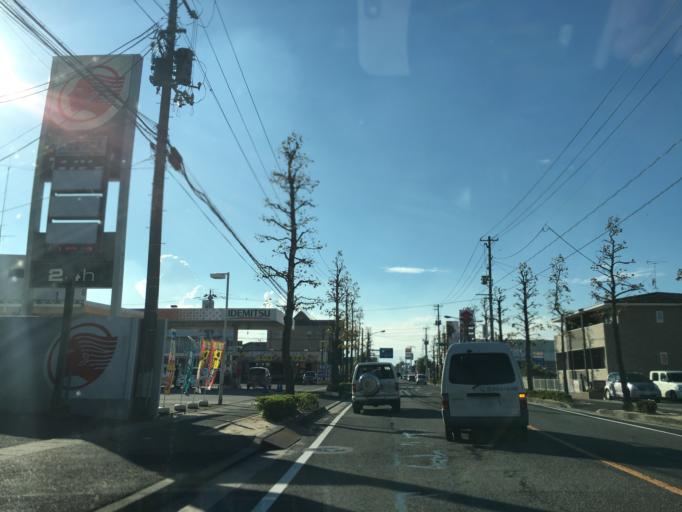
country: JP
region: Fukushima
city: Koriyama
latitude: 37.3980
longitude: 140.3445
